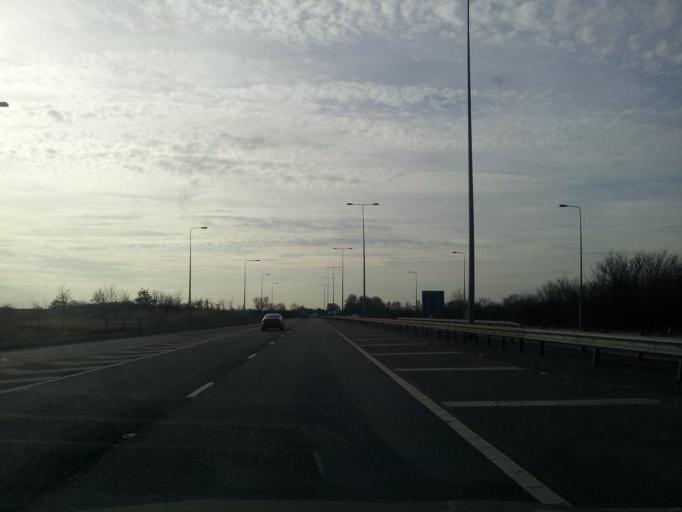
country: GB
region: England
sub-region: Cambridgeshire
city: Great Stukeley
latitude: 52.3595
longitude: -0.2543
